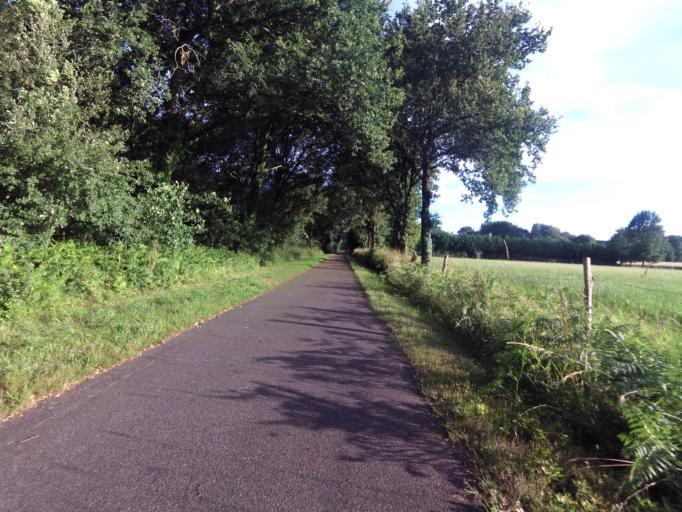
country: FR
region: Brittany
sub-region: Departement du Morbihan
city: Guillac
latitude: 47.8557
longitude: -2.4399
